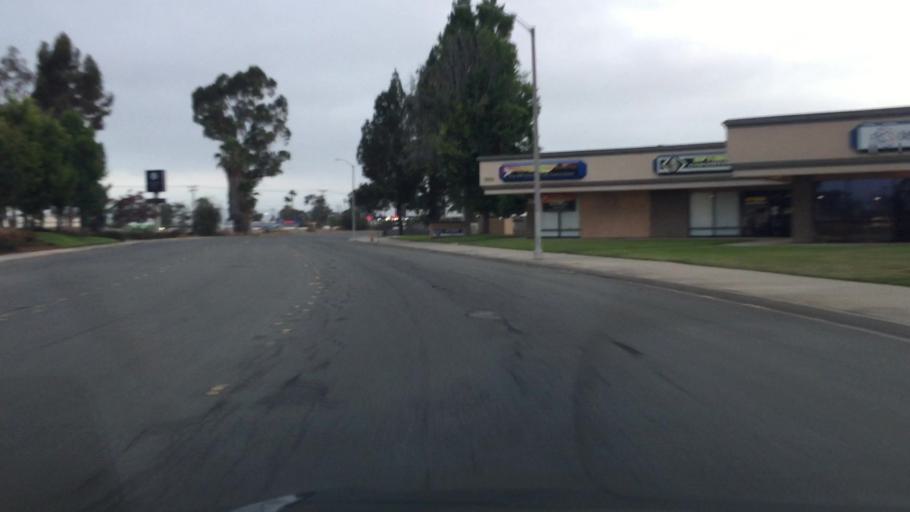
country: US
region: California
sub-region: San Diego County
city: El Cajon
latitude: 32.8095
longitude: -116.9605
